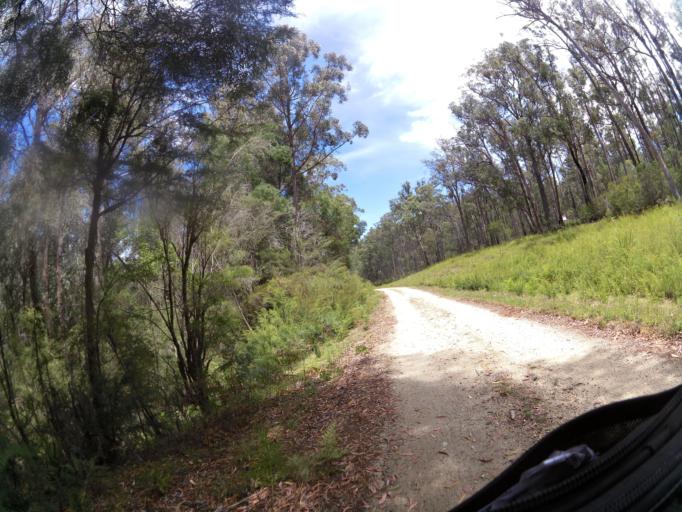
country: AU
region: Victoria
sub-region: East Gippsland
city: Lakes Entrance
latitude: -37.7431
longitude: 148.0410
